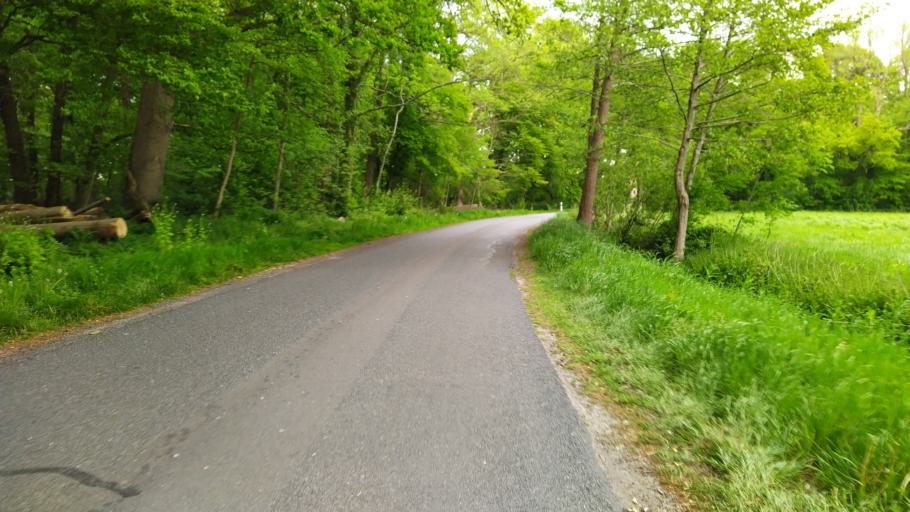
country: DE
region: Lower Saxony
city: Farven
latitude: 53.4022
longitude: 9.3578
